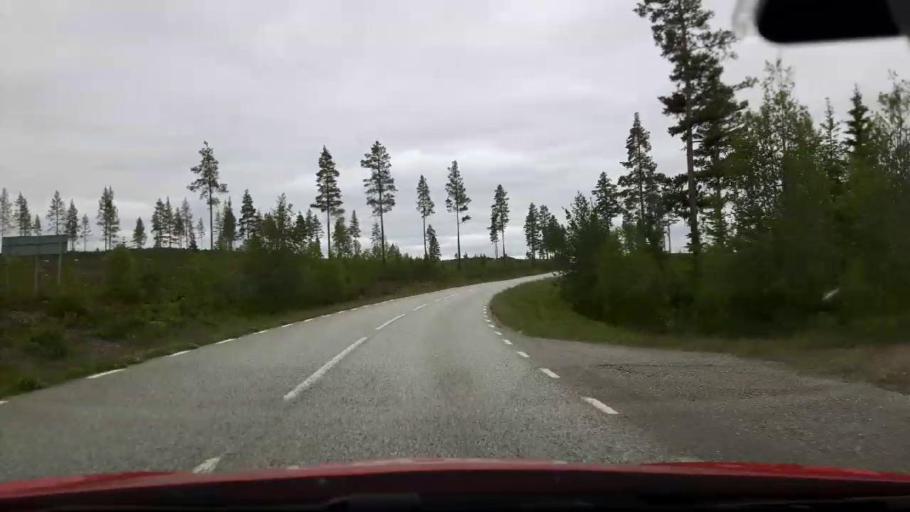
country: SE
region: Jaemtland
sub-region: Stroemsunds Kommun
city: Stroemsund
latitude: 63.3652
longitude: 15.7131
